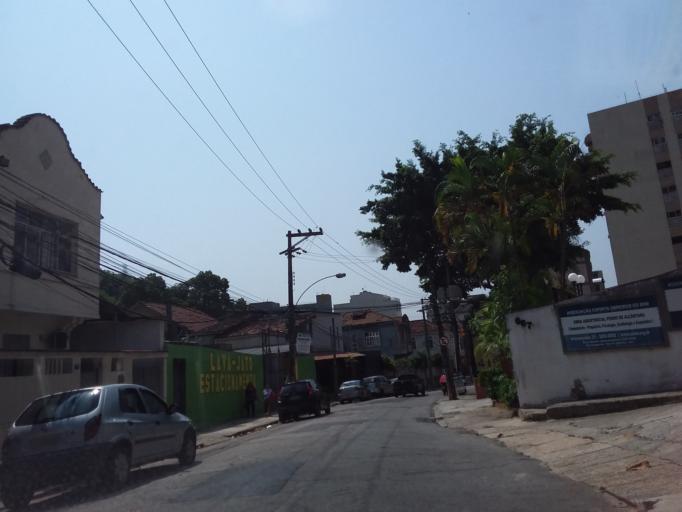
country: BR
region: Rio de Janeiro
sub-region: Rio De Janeiro
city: Rio de Janeiro
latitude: -22.9303
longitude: -43.2084
